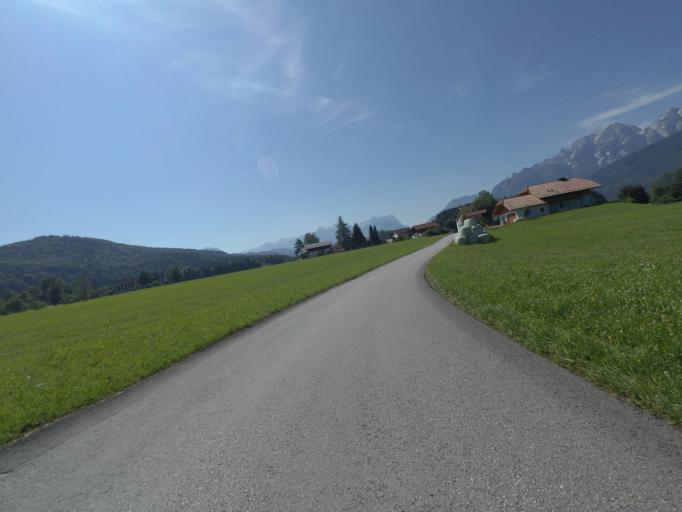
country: AT
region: Salzburg
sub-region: Politischer Bezirk Hallein
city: Adnet
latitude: 47.6635
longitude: 13.1476
